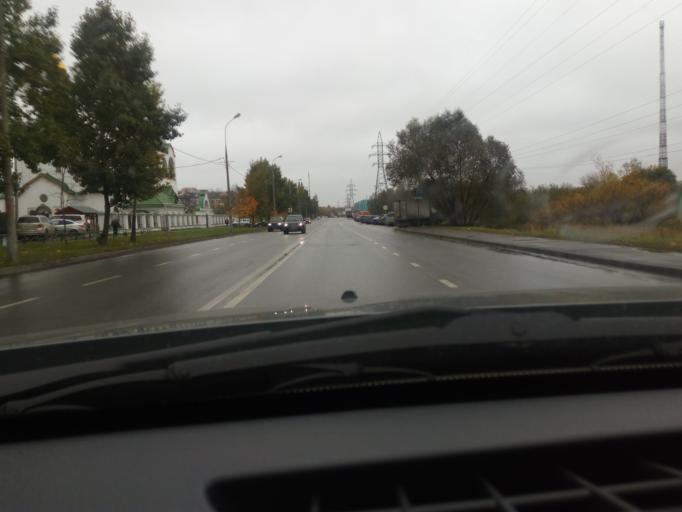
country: RU
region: Moskovskaya
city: Kuskovo
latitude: 55.7363
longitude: 37.8461
